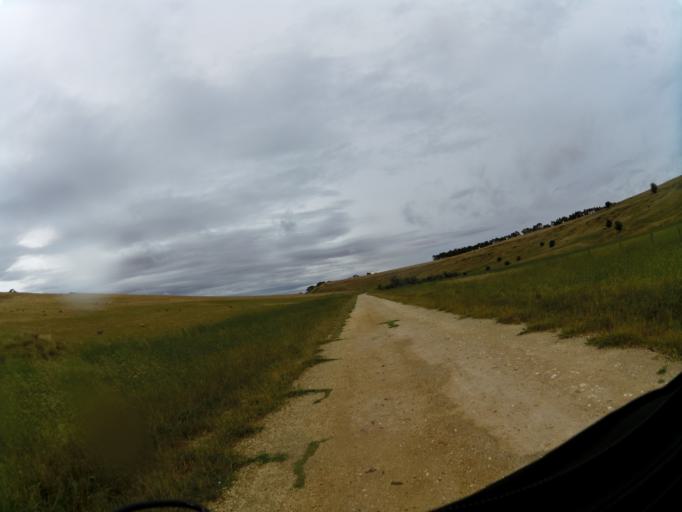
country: AU
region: Victoria
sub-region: Mount Alexander
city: Castlemaine
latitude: -37.2073
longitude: 144.0246
